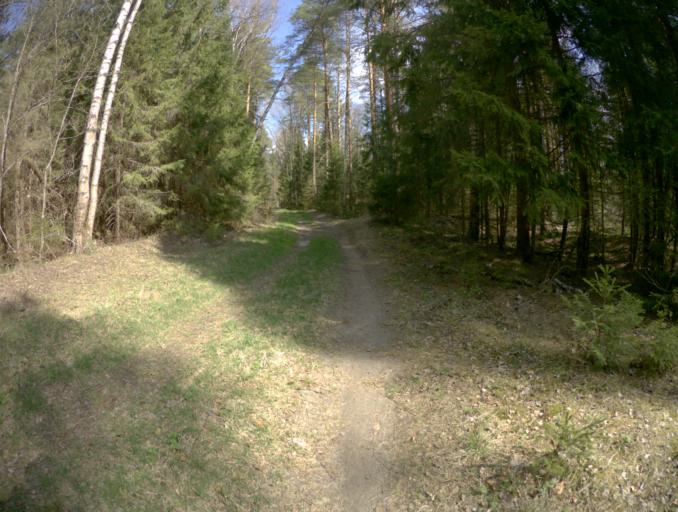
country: RU
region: Vladimir
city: Mezinovskiy
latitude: 55.5342
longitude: 40.2644
